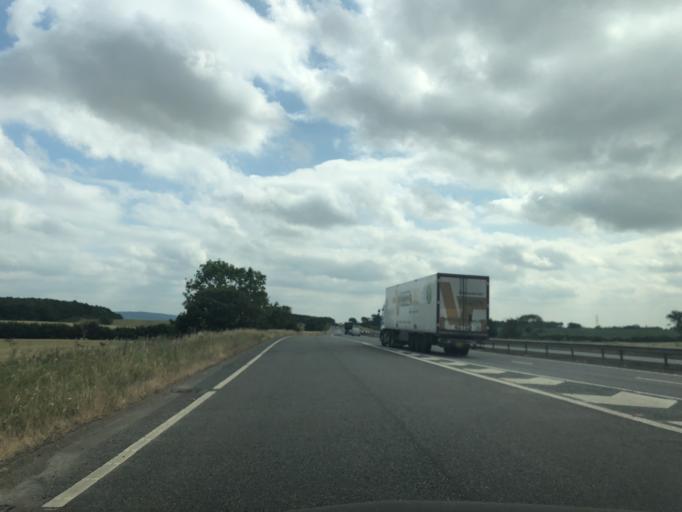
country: GB
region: England
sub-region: Stockton-on-Tees
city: Yarm
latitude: 54.4532
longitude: -1.3221
